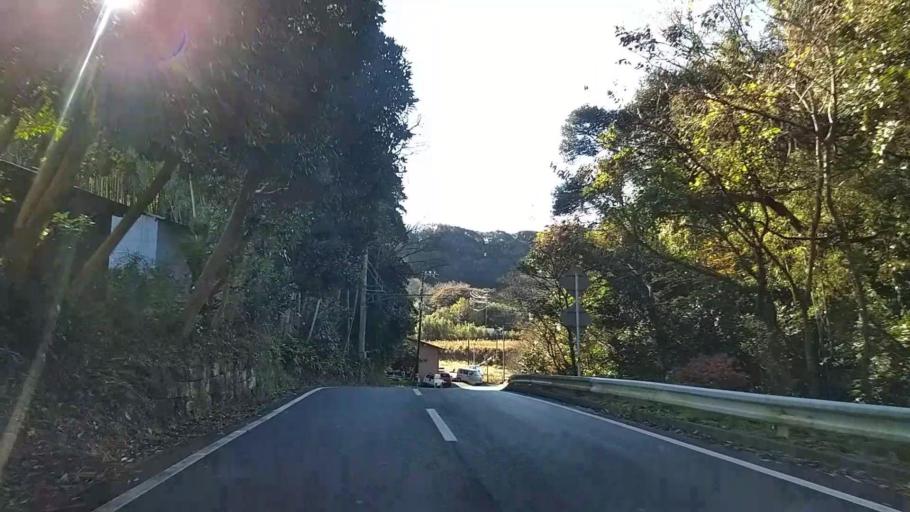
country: JP
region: Chiba
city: Futtsu
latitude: 35.2313
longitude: 139.8767
